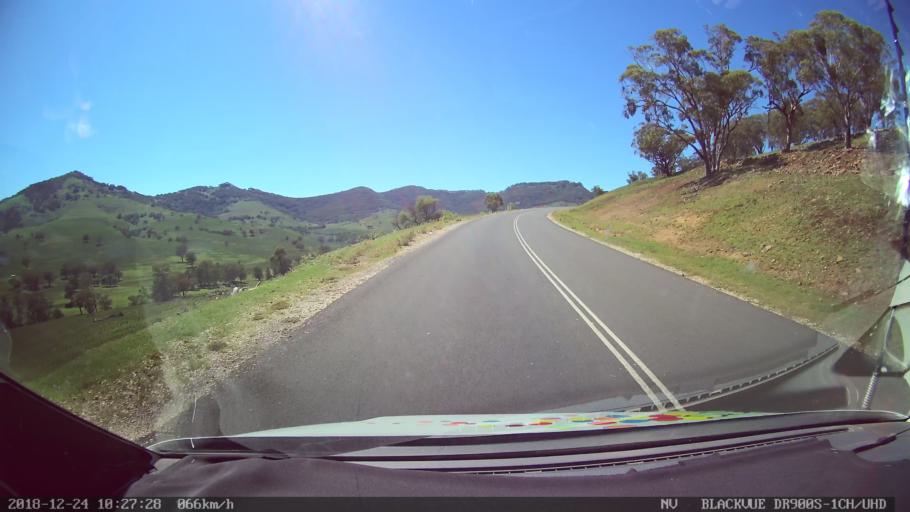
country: AU
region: New South Wales
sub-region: Liverpool Plains
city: Quirindi
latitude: -31.8179
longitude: 150.5328
